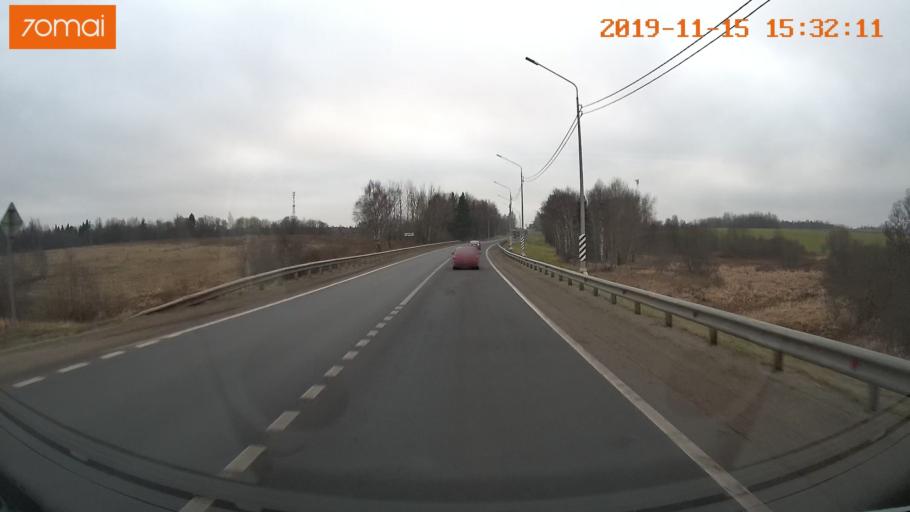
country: RU
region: Jaroslavl
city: Danilov
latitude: 58.0925
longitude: 40.1026
